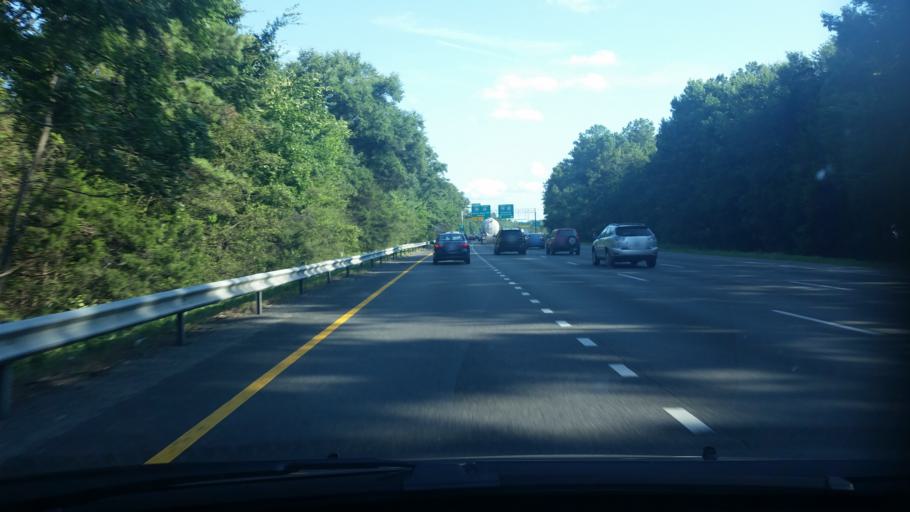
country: US
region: Virginia
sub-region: Henrico County
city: Chamberlayne
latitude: 37.6749
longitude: -77.4490
